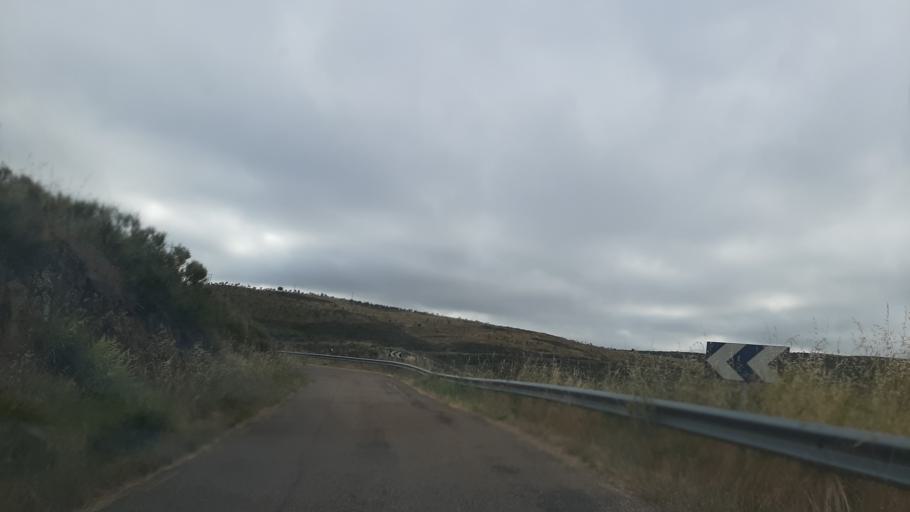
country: ES
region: Castille and Leon
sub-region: Provincia de Salamanca
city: Zamarra
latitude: 40.5300
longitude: -6.4796
